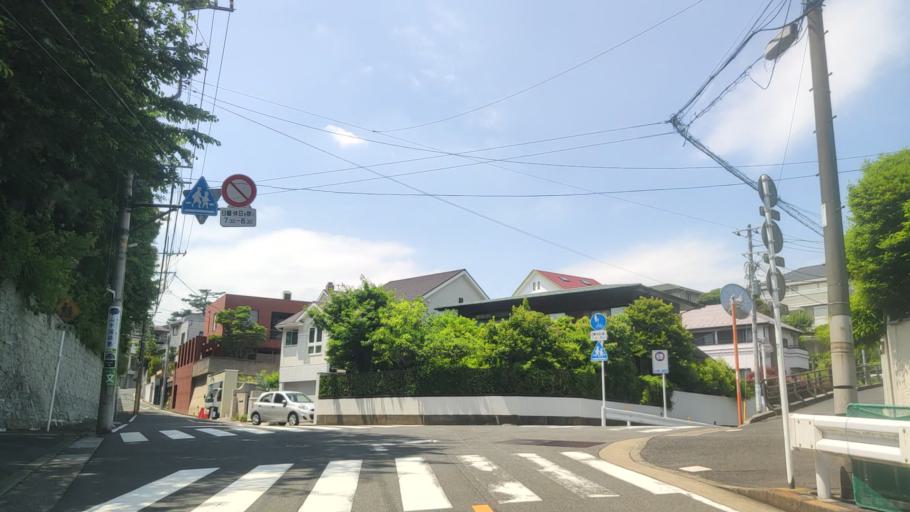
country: JP
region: Kanagawa
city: Yokohama
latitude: 35.4366
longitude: 139.6495
